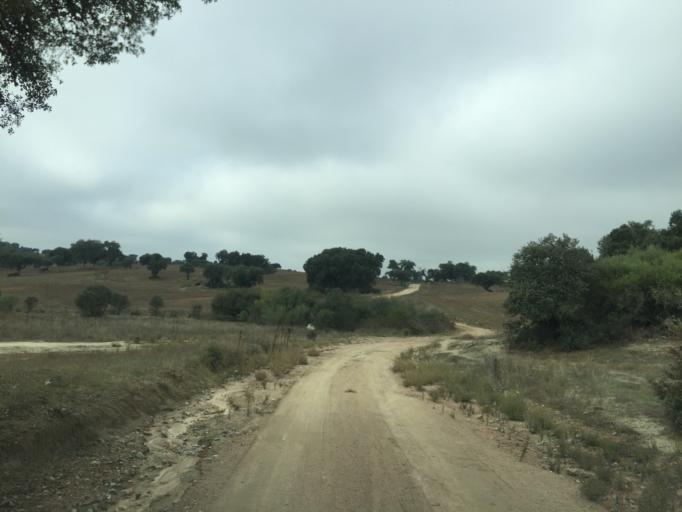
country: PT
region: Portalegre
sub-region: Fronteira
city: Fronteira
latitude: 39.0689
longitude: -7.6052
